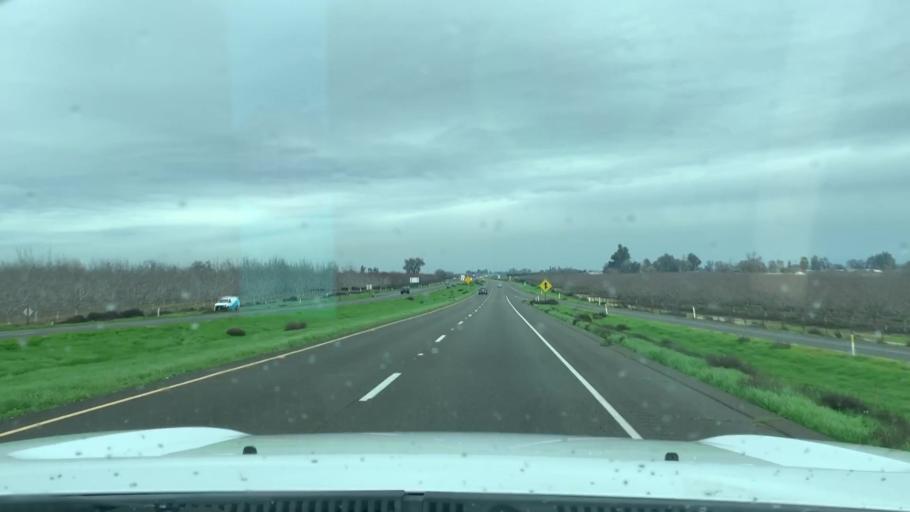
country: US
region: California
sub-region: Fresno County
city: Riverdale
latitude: 36.4034
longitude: -119.8066
